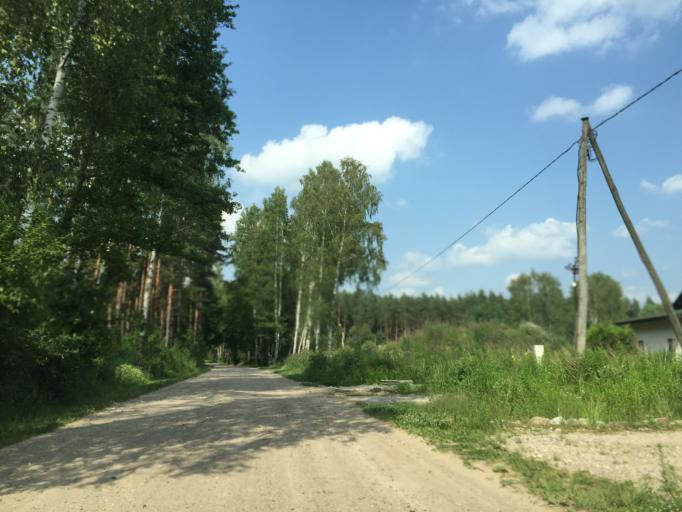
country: LV
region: Ozolnieku
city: Ozolnieki
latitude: 56.6735
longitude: 23.7574
